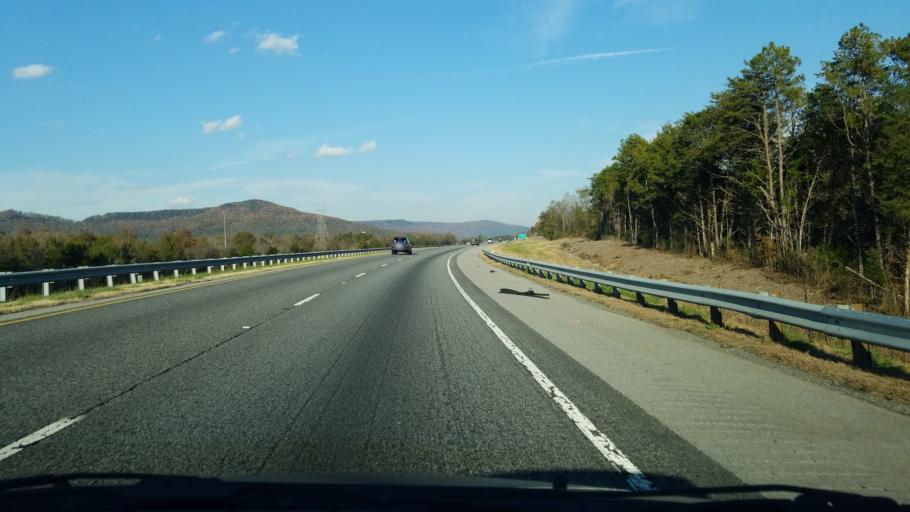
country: US
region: Georgia
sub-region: Dade County
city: Trenton
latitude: 34.9365
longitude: -85.4824
